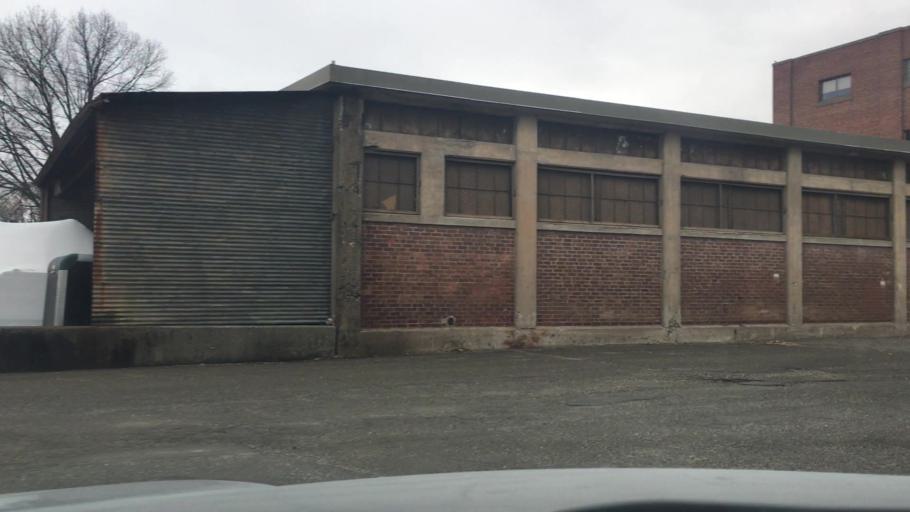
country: US
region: Massachusetts
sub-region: Hampden County
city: North Chicopee
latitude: 42.1930
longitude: -72.5992
